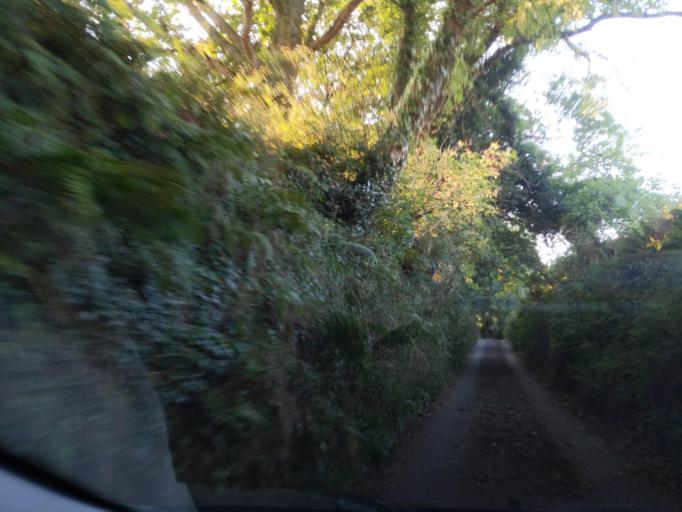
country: GB
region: England
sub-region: Cornwall
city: Fowey
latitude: 50.3670
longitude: -4.5924
